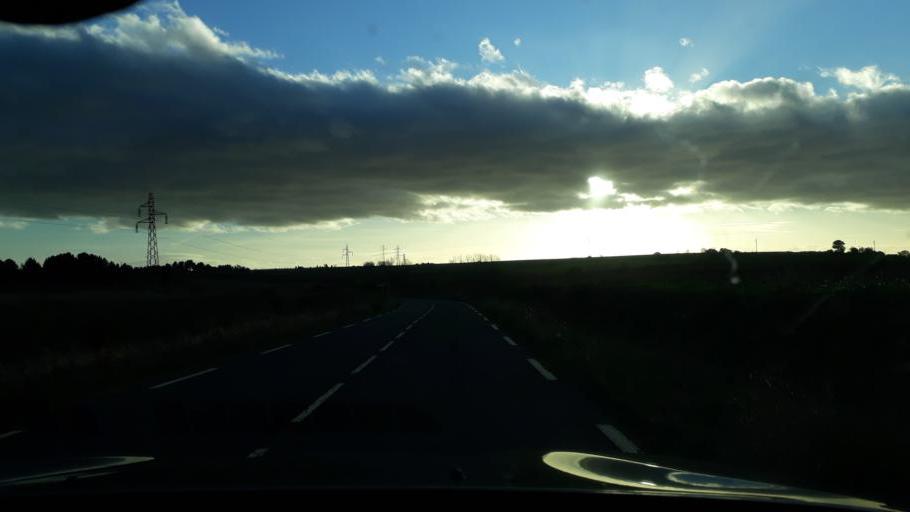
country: FR
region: Languedoc-Roussillon
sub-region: Departement de l'Herault
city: Nissan-lez-Enserune
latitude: 43.3008
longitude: 3.1338
